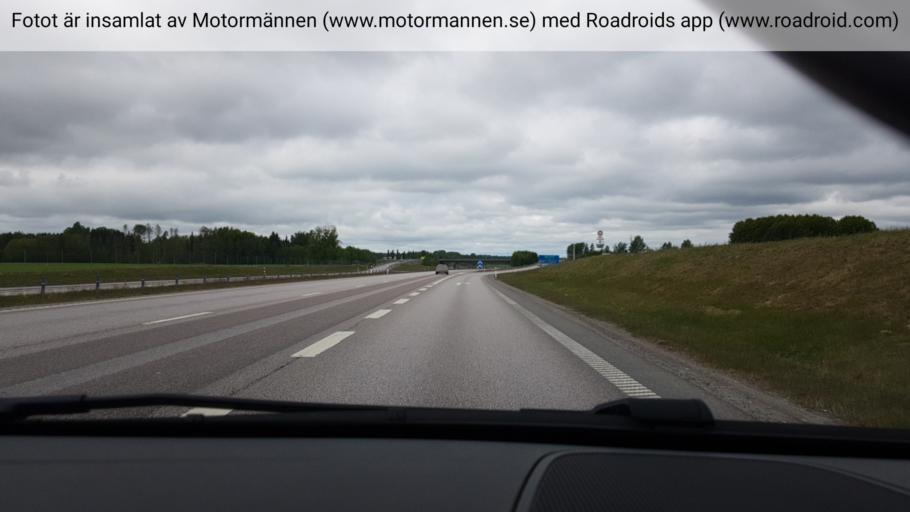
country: SE
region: Uppsala
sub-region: Tierps Kommun
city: Tierp
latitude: 60.3360
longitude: 17.4921
